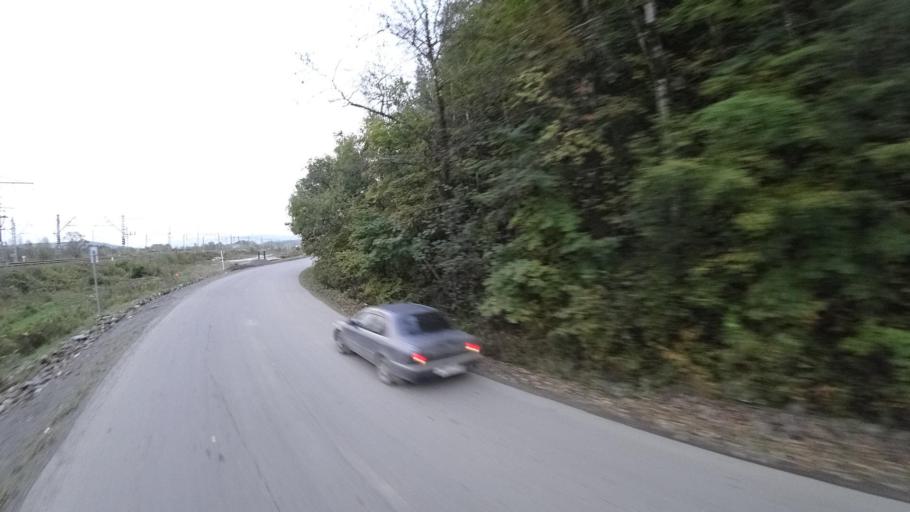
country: RU
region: Jewish Autonomous Oblast
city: Izvestkovyy
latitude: 48.9913
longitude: 131.5381
